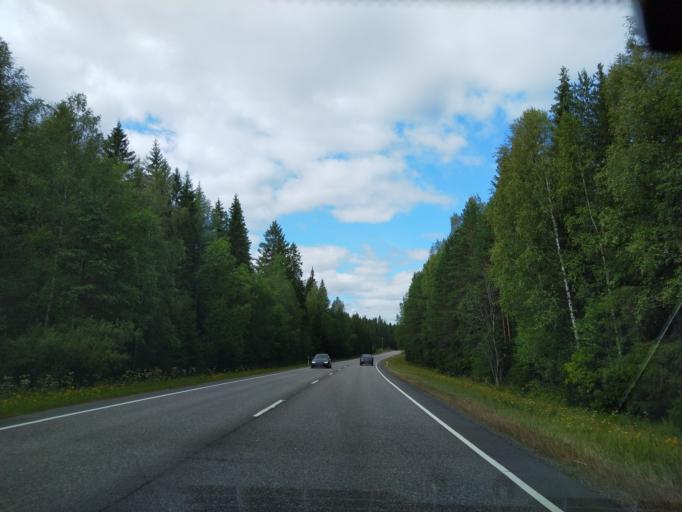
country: FI
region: Haeme
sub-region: Riihimaeki
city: Loppi
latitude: 60.7494
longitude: 24.3197
